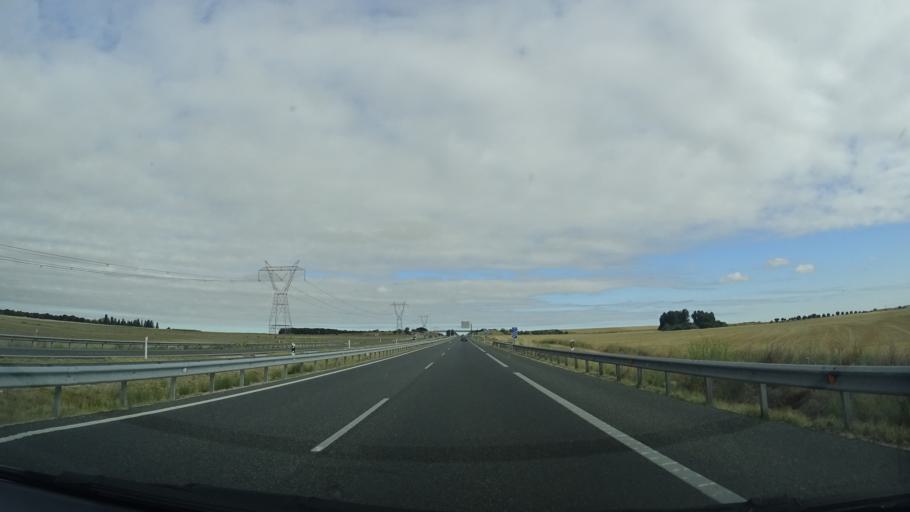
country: ES
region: Castille and Leon
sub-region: Provincia de Valladolid
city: San Pablo de la Moraleja
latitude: 41.1437
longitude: -4.7845
